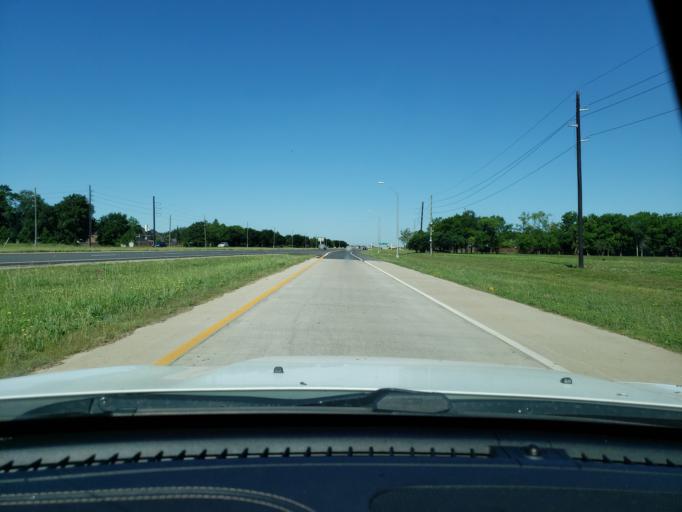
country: US
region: Texas
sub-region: Fort Bend County
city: Pecan Grove
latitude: 29.6606
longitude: -95.7243
